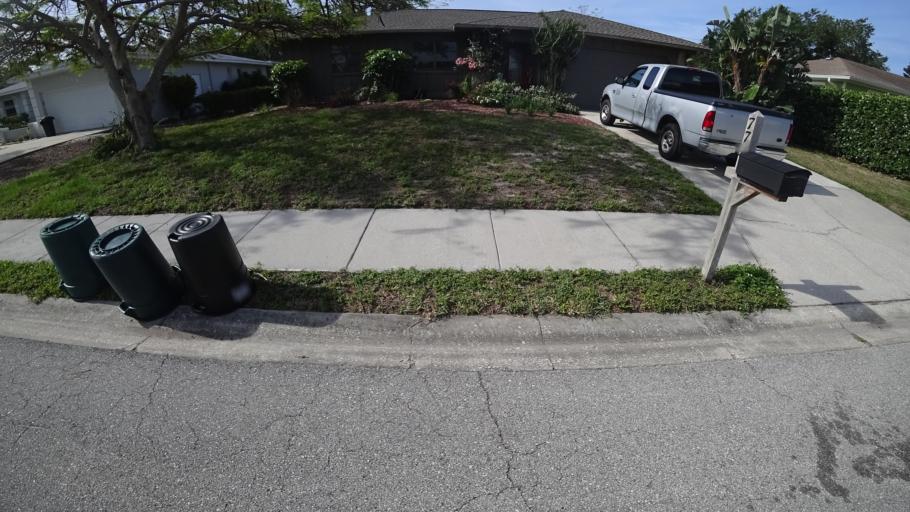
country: US
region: Florida
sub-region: Manatee County
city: West Bradenton
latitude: 27.5076
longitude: -82.6397
